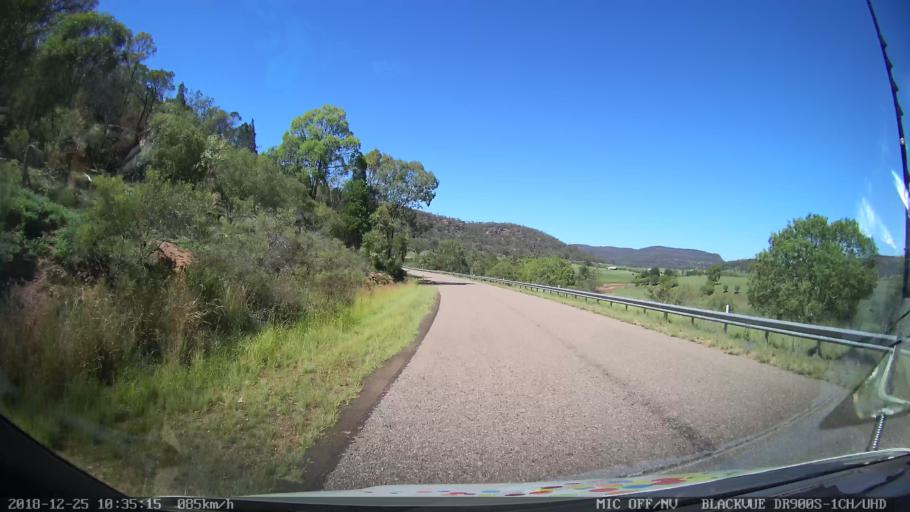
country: AU
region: New South Wales
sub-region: Upper Hunter Shire
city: Merriwa
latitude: -32.3966
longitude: 150.3974
